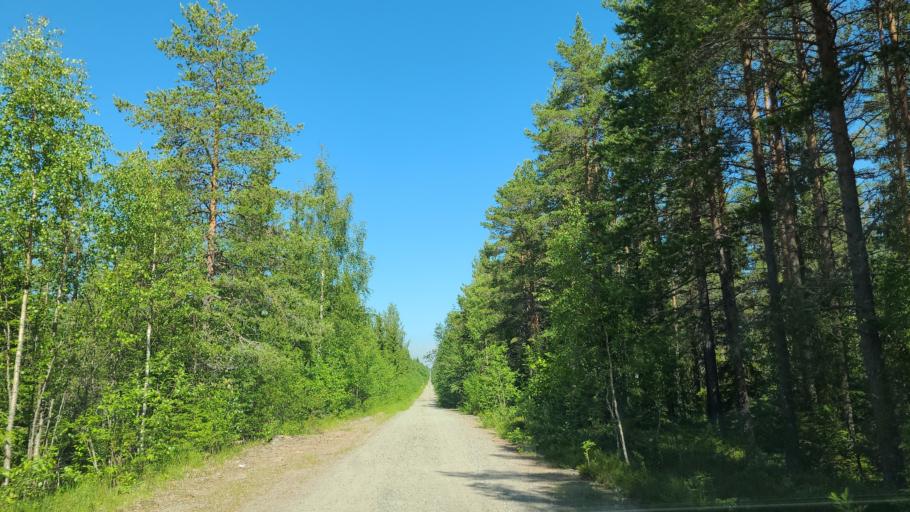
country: SE
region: Vaesternorrland
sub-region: OErnskoeldsviks Kommun
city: Husum
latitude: 63.4182
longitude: 19.2220
